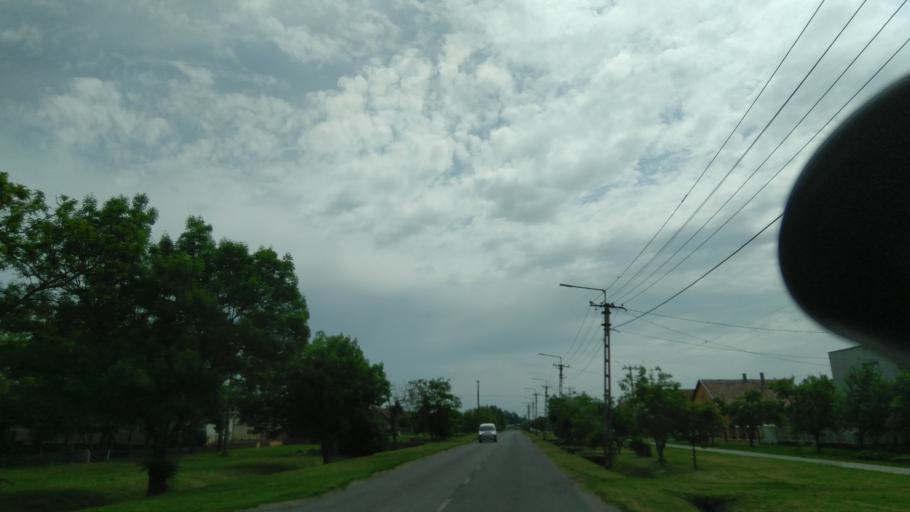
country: HU
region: Bekes
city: Fuzesgyarmat
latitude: 47.1022
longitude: 21.2180
